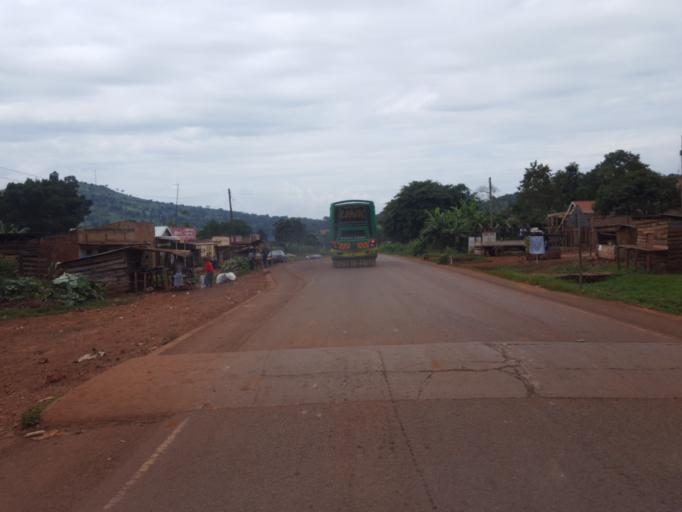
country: UG
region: Central Region
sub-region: Mityana District
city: Mityana
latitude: 0.6616
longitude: 32.0911
